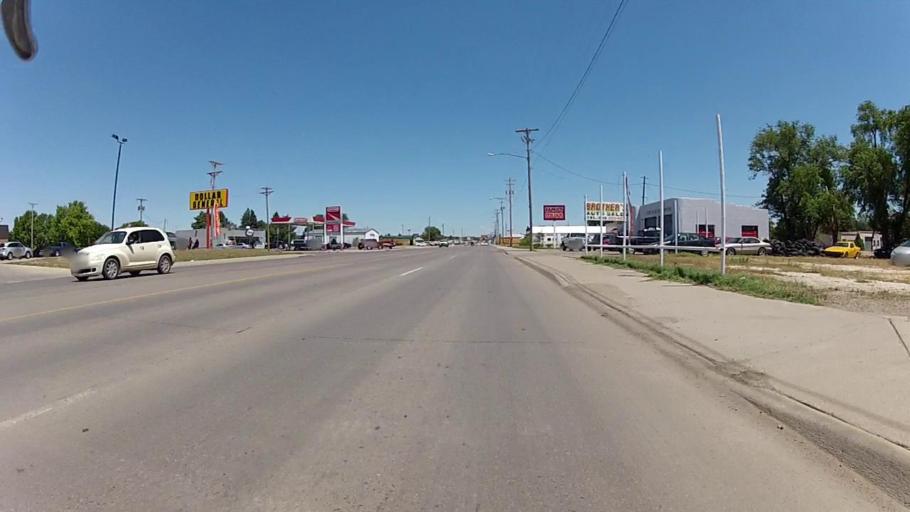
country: US
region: Kansas
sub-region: Ford County
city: Dodge City
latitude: 37.7389
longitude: -100.0194
